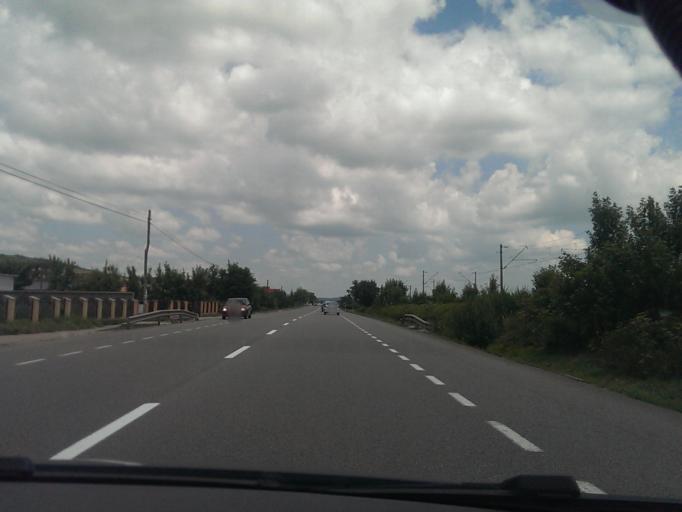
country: RO
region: Cluj
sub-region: Comuna Apahida
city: Apahida
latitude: 46.8480
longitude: 23.7537
